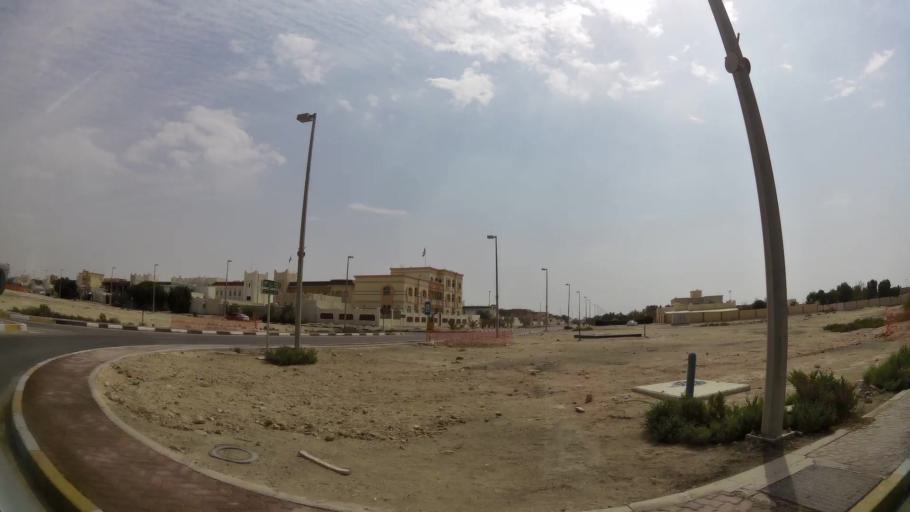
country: AE
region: Abu Dhabi
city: Abu Dhabi
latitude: 24.5315
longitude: 54.6811
